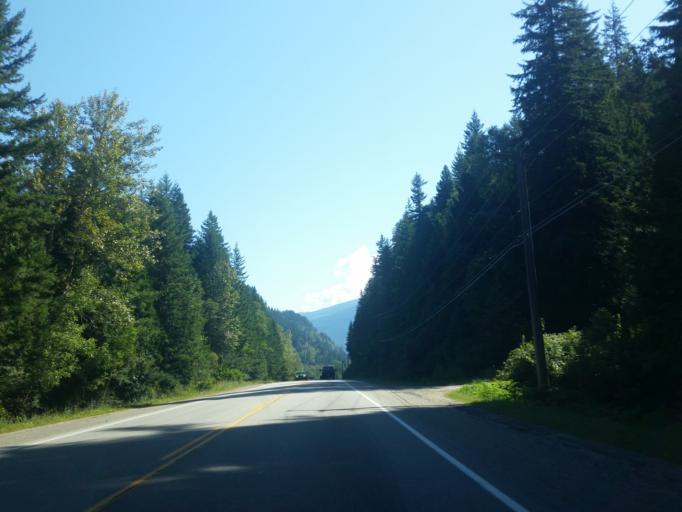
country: CA
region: British Columbia
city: Sicamous
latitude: 50.8895
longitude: -118.8777
